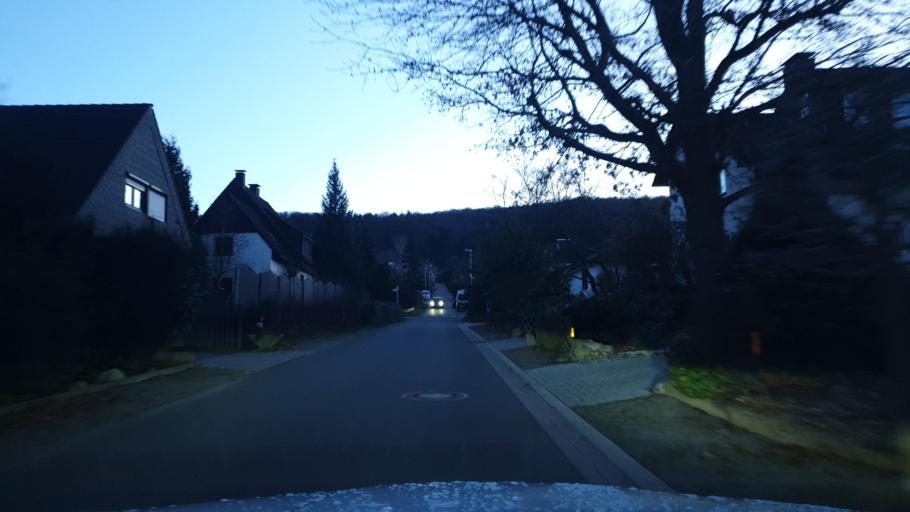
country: DE
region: North Rhine-Westphalia
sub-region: Regierungsbezirk Detmold
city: Minden
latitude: 52.2602
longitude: 8.8641
